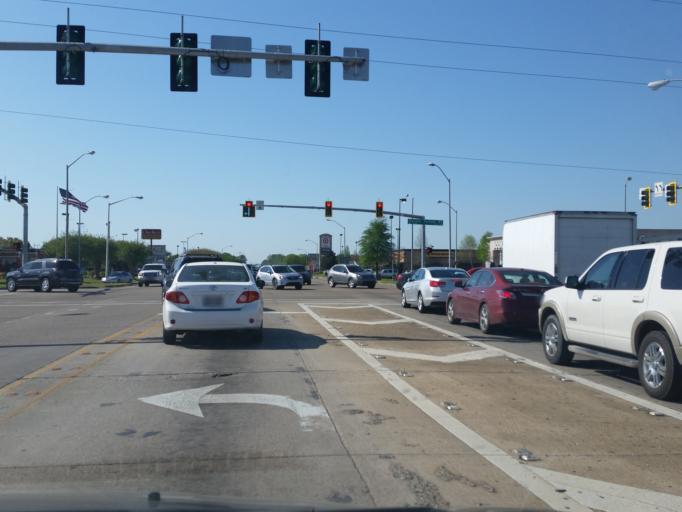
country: US
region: Louisiana
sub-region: Lafayette Parish
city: Milton
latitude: 30.1562
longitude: -92.0480
